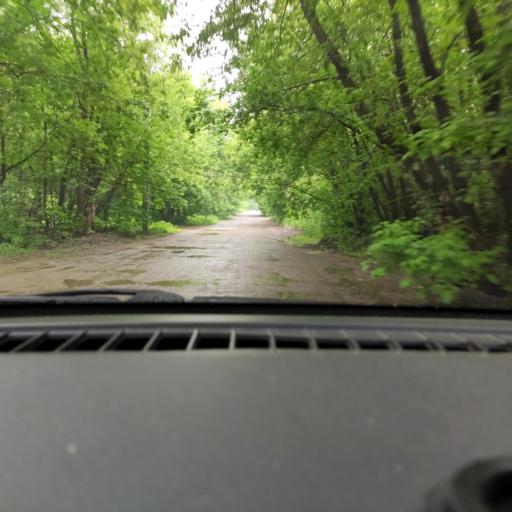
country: RU
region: Perm
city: Overyata
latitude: 57.9986
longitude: 55.9264
